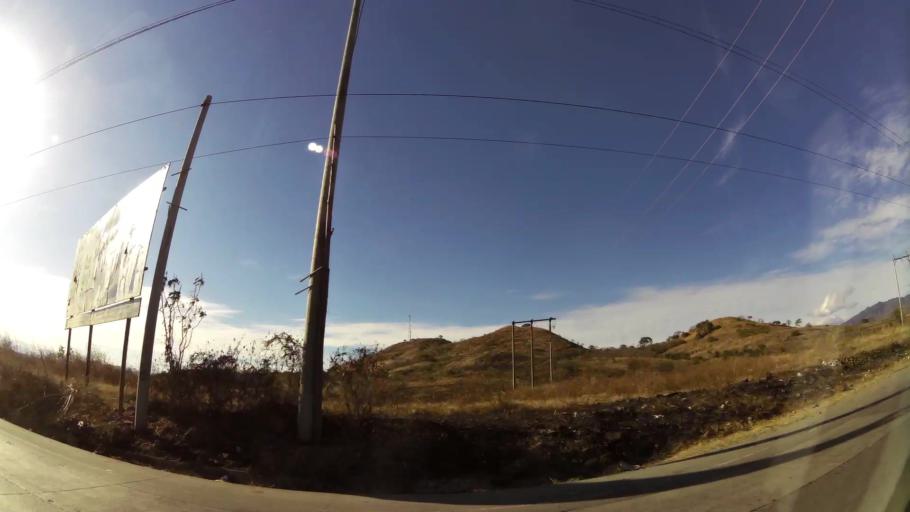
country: SV
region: Santa Ana
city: Metapan
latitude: 14.3154
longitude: -89.4479
